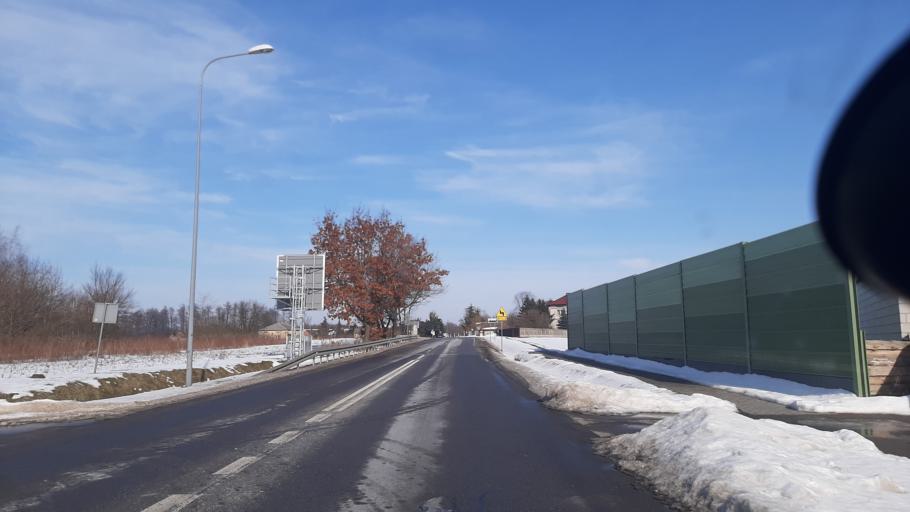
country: PL
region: Lublin Voivodeship
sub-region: Powiat pulawski
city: Kurow
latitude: 51.4072
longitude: 22.2047
